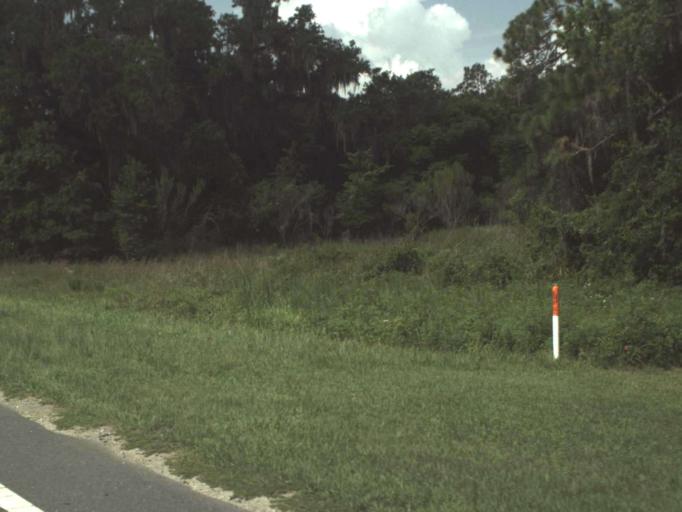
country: US
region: Florida
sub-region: Sumter County
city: Wildwood
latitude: 28.8104
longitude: -82.0456
